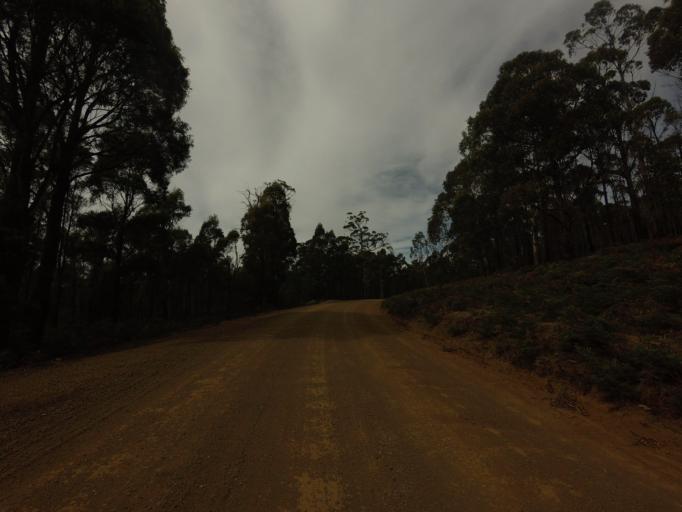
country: AU
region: Tasmania
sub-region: Sorell
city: Sorell
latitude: -42.5114
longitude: 147.6448
